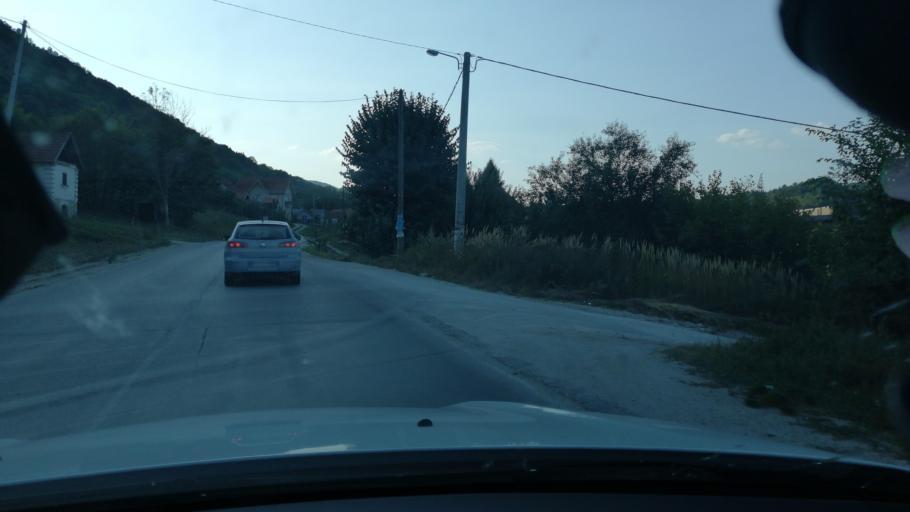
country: RS
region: Central Serbia
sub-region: Moravicki Okrug
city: Lucani
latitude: 43.7666
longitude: 20.2384
